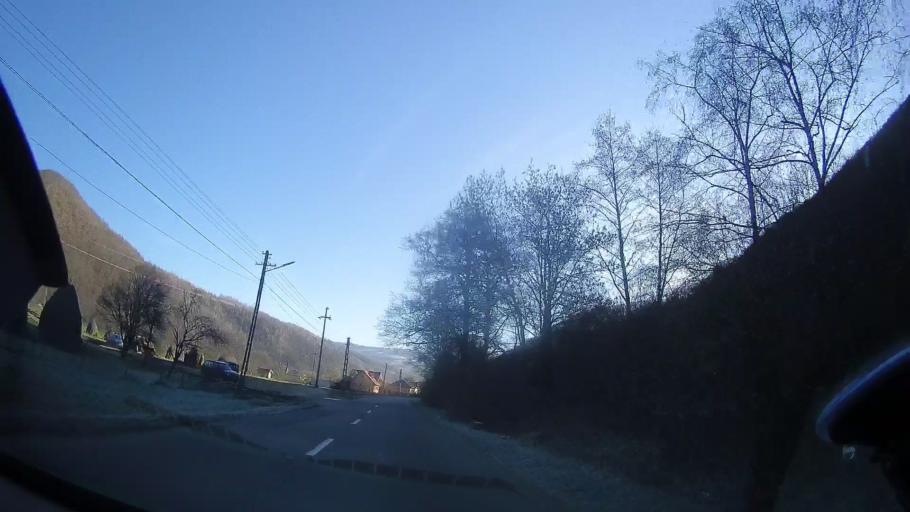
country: RO
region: Bihor
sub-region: Comuna Bulz
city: Bulz
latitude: 46.9096
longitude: 22.6778
